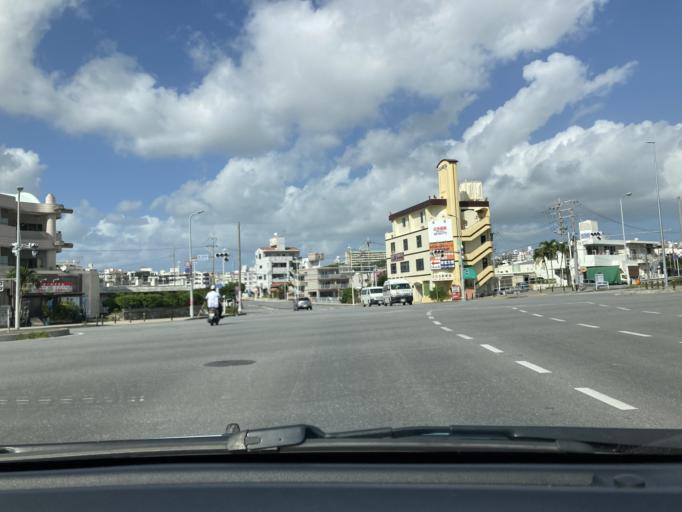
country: JP
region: Okinawa
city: Tomigusuku
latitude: 26.1935
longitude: 127.6951
